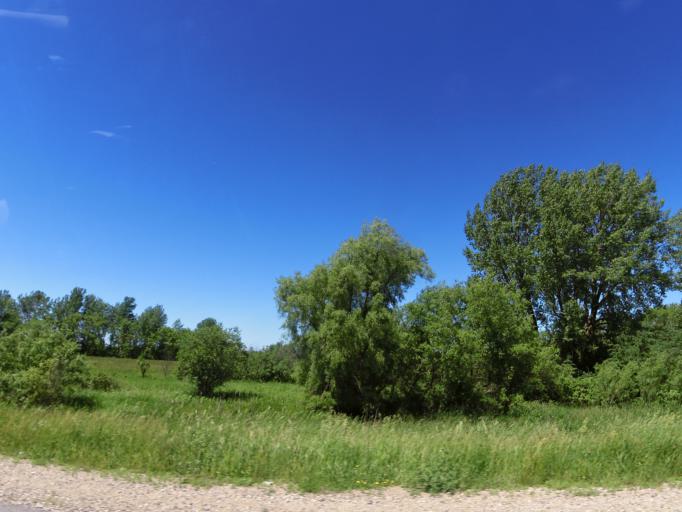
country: US
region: Minnesota
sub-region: Becker County
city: Detroit Lakes
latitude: 47.0368
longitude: -95.9123
